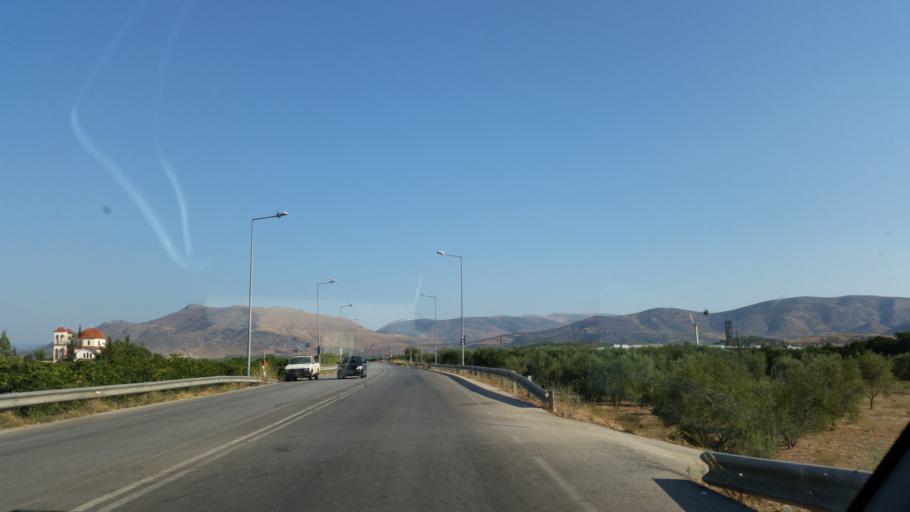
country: GR
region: Peloponnese
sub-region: Nomos Argolidos
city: Ayia Trias
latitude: 37.6349
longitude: 22.8172
